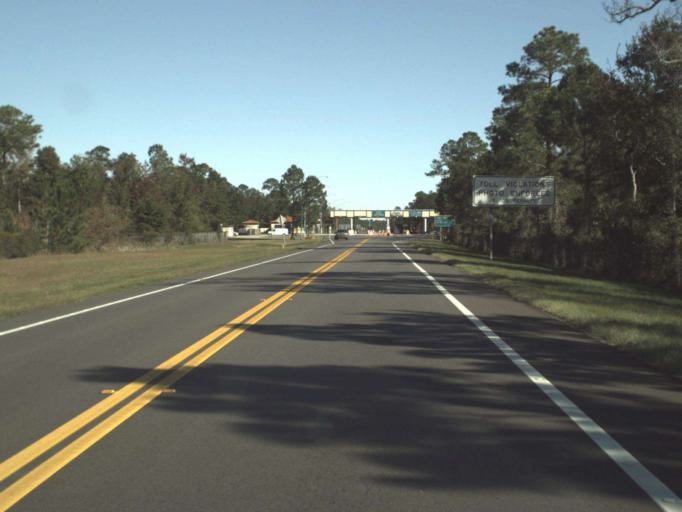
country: US
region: Florida
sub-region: Santa Rosa County
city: Oriole Beach
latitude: 30.4533
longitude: -87.0968
